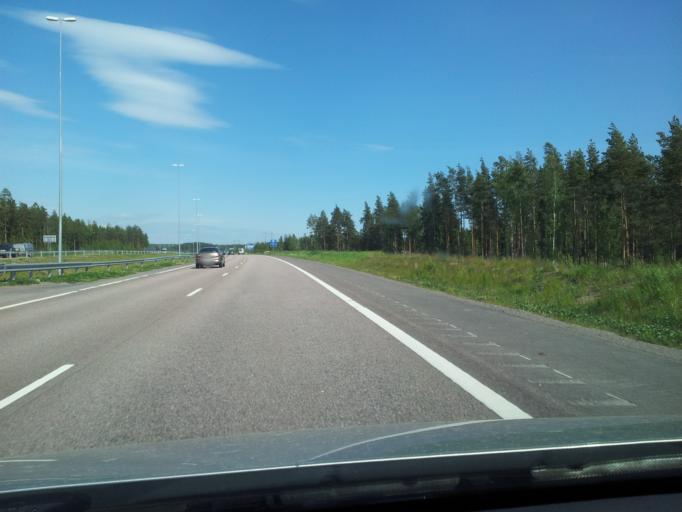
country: FI
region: Uusimaa
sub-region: Loviisa
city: Lovisa
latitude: 60.4587
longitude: 26.1771
